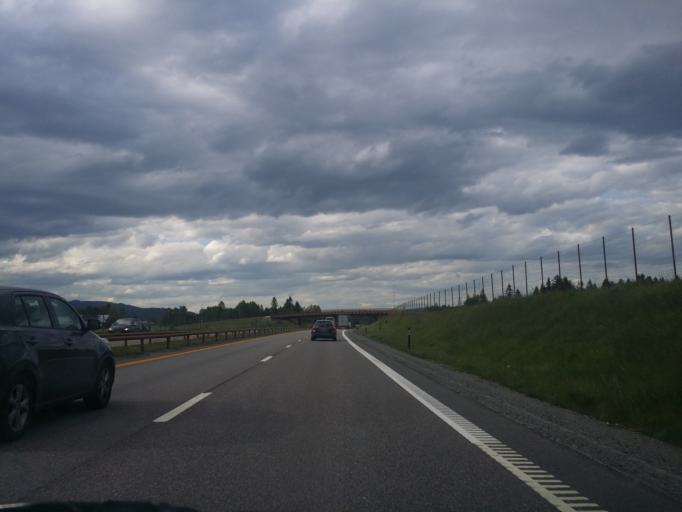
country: NO
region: Akershus
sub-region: Eidsvoll
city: Eidsvoll
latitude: 60.3673
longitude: 11.2042
